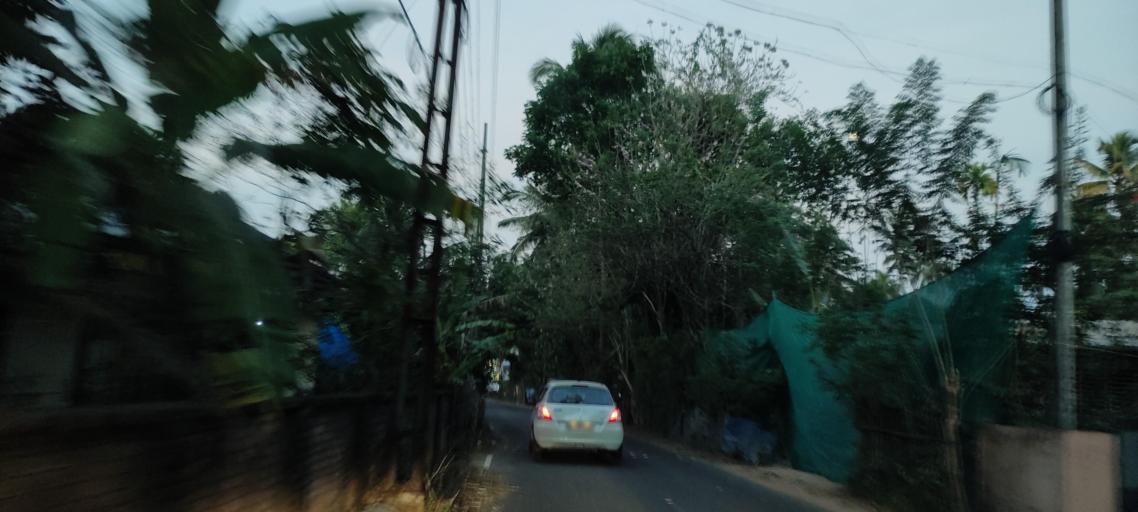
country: IN
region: Kerala
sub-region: Alappuzha
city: Kutiatodu
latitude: 9.7696
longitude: 76.3249
